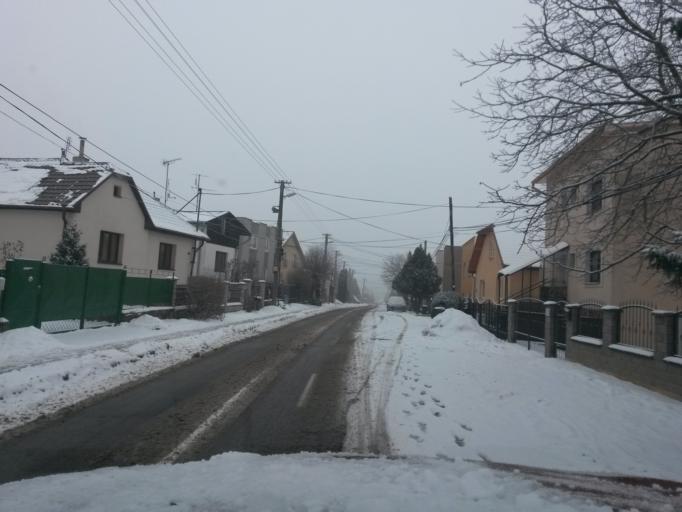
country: SK
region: Kosicky
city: Kosice
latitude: 48.7321
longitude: 21.2999
